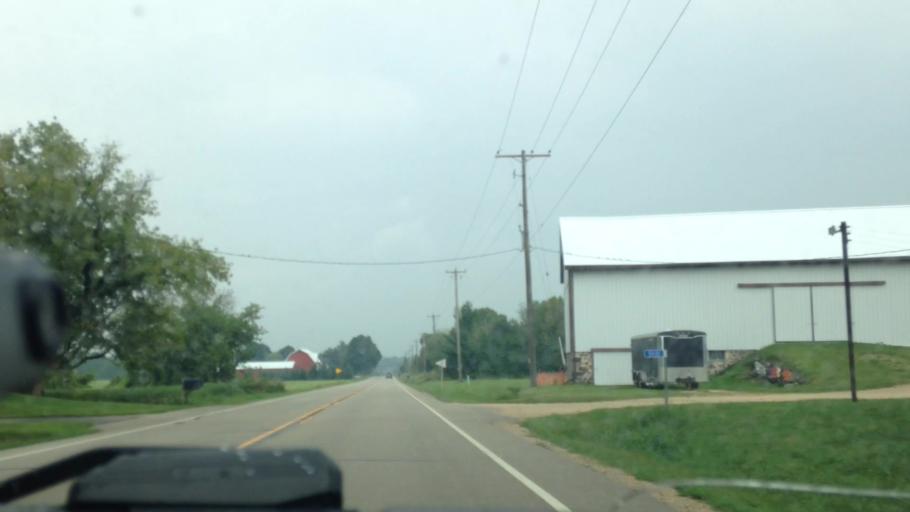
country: US
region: Wisconsin
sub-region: Washington County
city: Hartford
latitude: 43.4107
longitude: -88.3706
